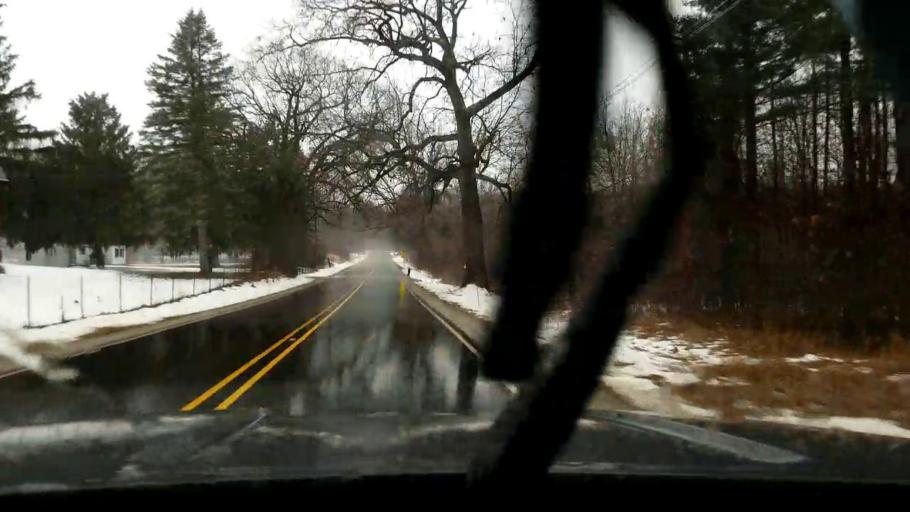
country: US
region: Michigan
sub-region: Jackson County
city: Michigan Center
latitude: 42.3165
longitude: -84.3071
